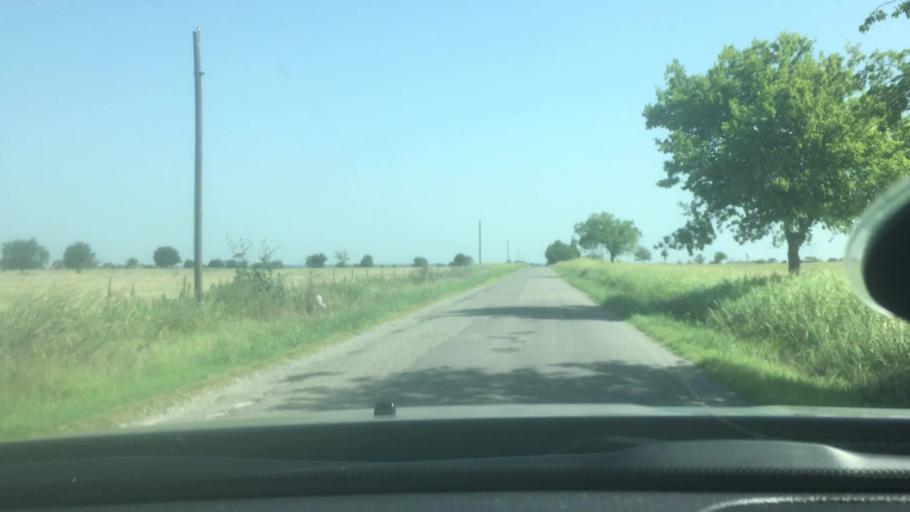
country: US
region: Oklahoma
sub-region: Bryan County
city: Calera
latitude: 33.9596
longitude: -96.4656
